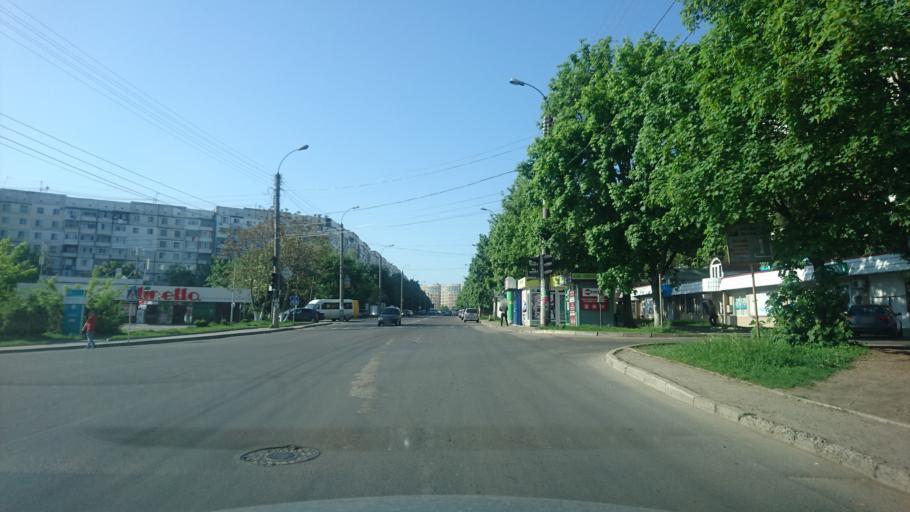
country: MD
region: Chisinau
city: Vatra
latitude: 47.0433
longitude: 28.7702
